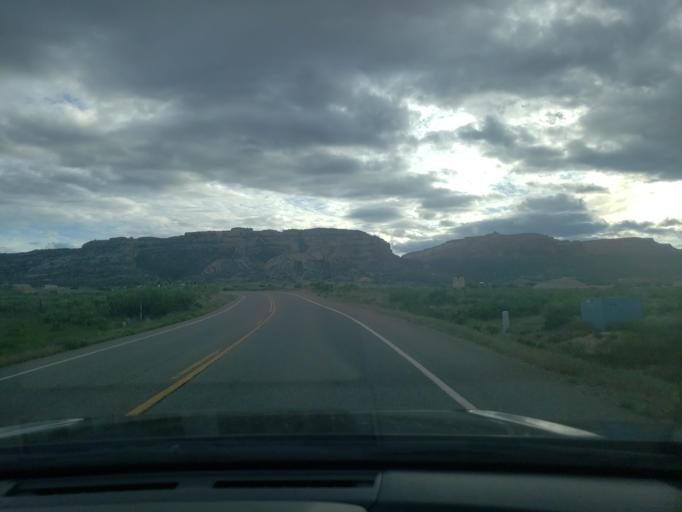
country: US
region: Colorado
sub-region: Mesa County
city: Redlands
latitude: 39.0455
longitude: -108.6225
